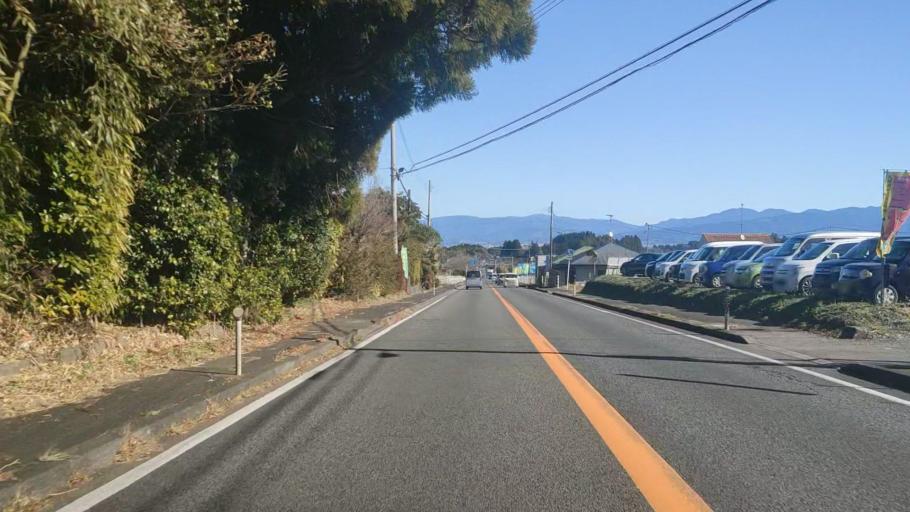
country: JP
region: Kagoshima
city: Sueyoshicho-ninokata
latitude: 31.7010
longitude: 131.0159
